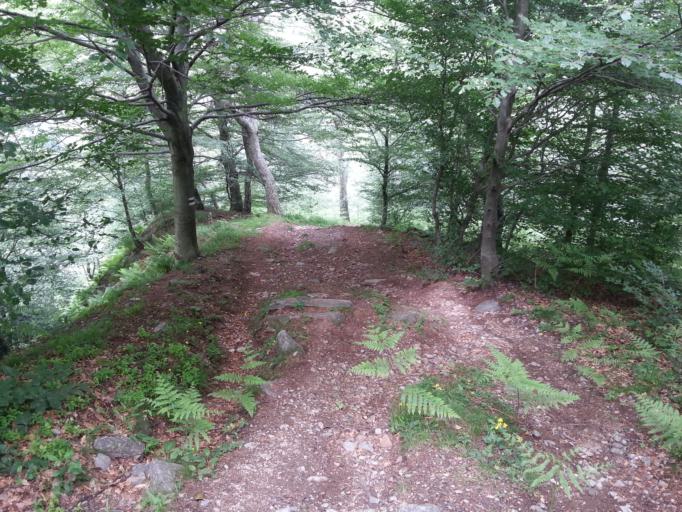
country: CH
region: Ticino
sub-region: Lugano District
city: Tesserete
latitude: 46.1083
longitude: 8.9683
